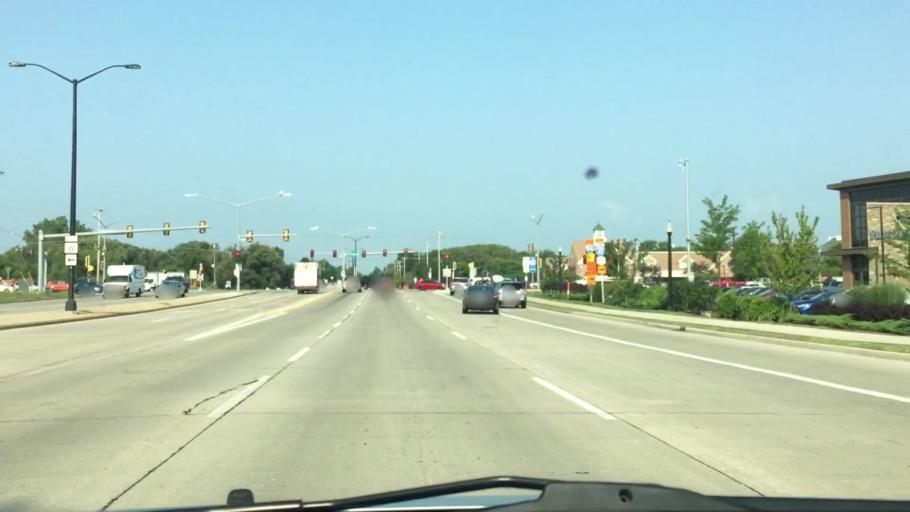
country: US
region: Wisconsin
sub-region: Waukesha County
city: Elm Grove
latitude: 43.0168
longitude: -88.1056
